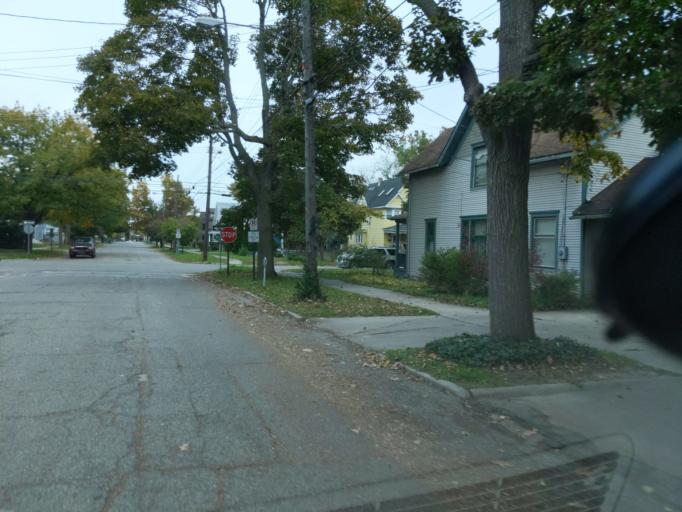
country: US
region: Michigan
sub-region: Ingham County
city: Lansing
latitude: 42.7399
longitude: -84.5574
